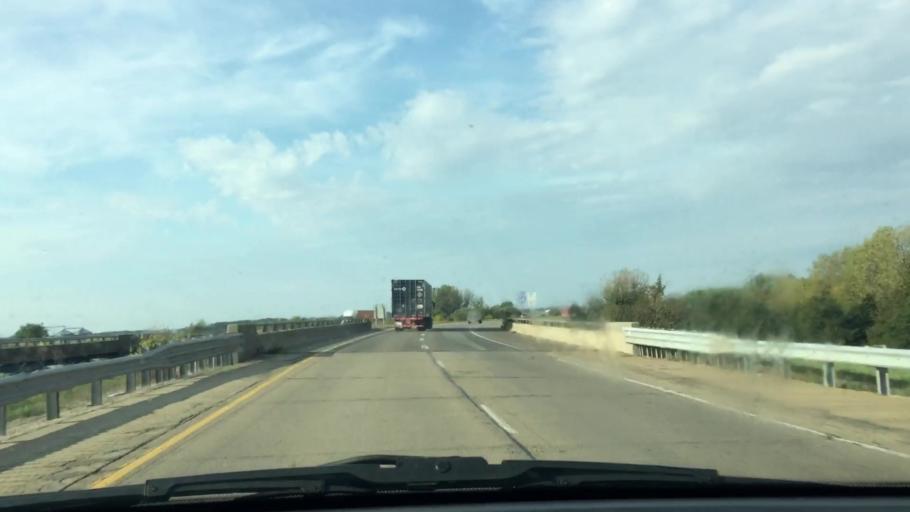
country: US
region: Illinois
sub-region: Whiteside County
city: Rock Falls
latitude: 41.7533
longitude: -89.6435
